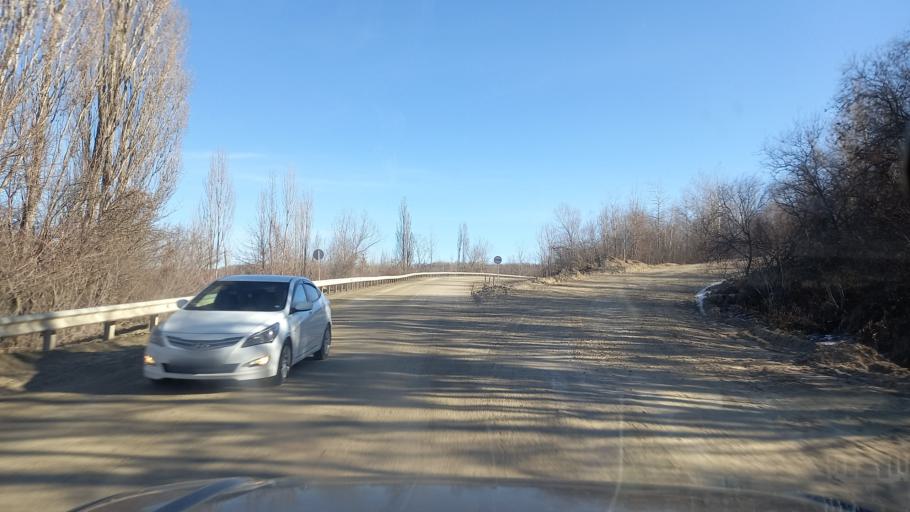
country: RU
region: Adygeya
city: Kamennomostskiy
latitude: 44.2765
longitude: 40.2243
